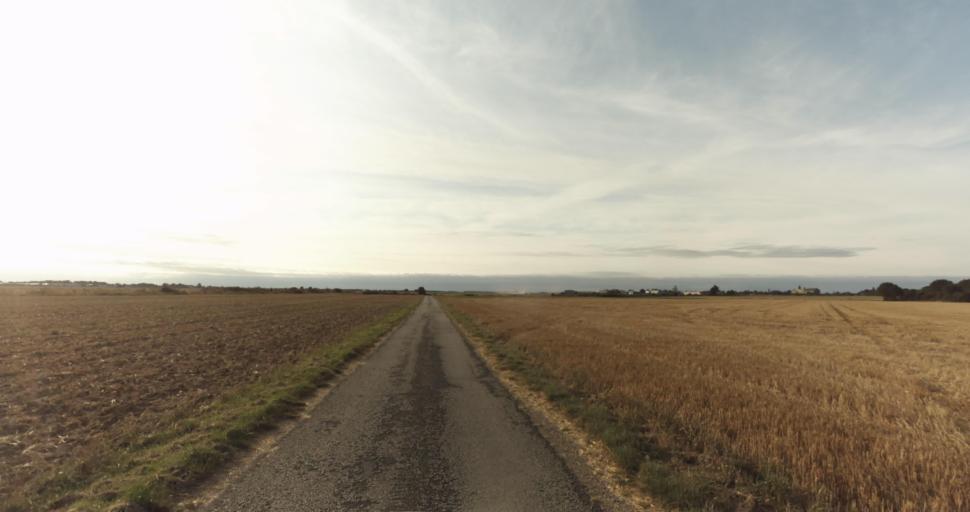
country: FR
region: Haute-Normandie
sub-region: Departement de l'Eure
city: Marcilly-sur-Eure
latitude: 48.8881
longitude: 1.2764
